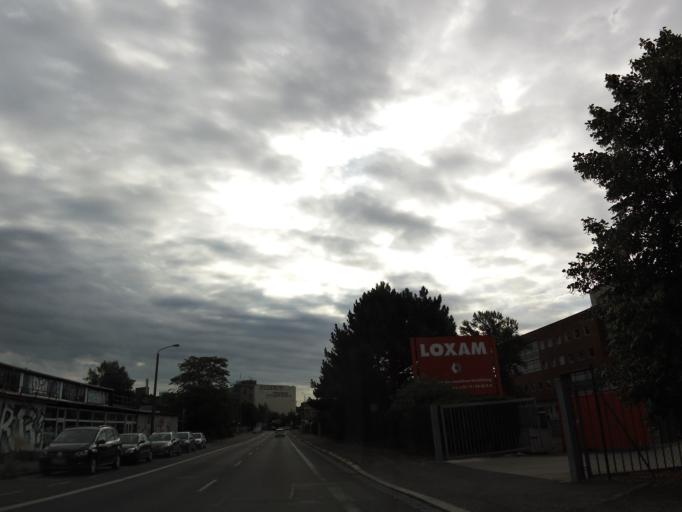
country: DE
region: Saxony
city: Leipzig
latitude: 51.3261
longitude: 12.3122
